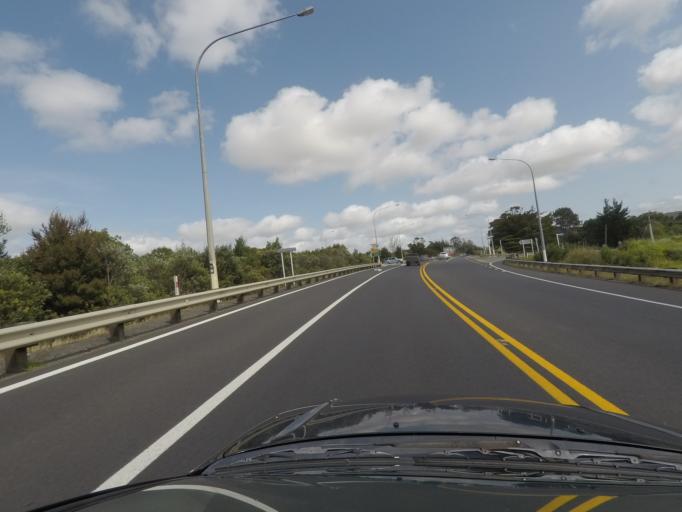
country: NZ
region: Northland
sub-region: Whangarei
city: Whangarei
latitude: -35.8334
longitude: 174.3162
